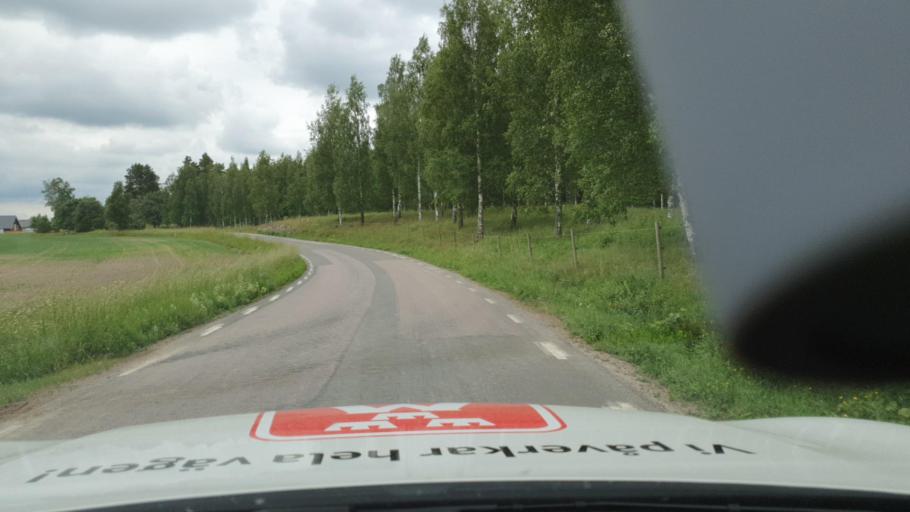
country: SE
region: Vaestra Goetaland
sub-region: Tidaholms Kommun
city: Olofstorp
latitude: 58.2715
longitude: 14.1007
